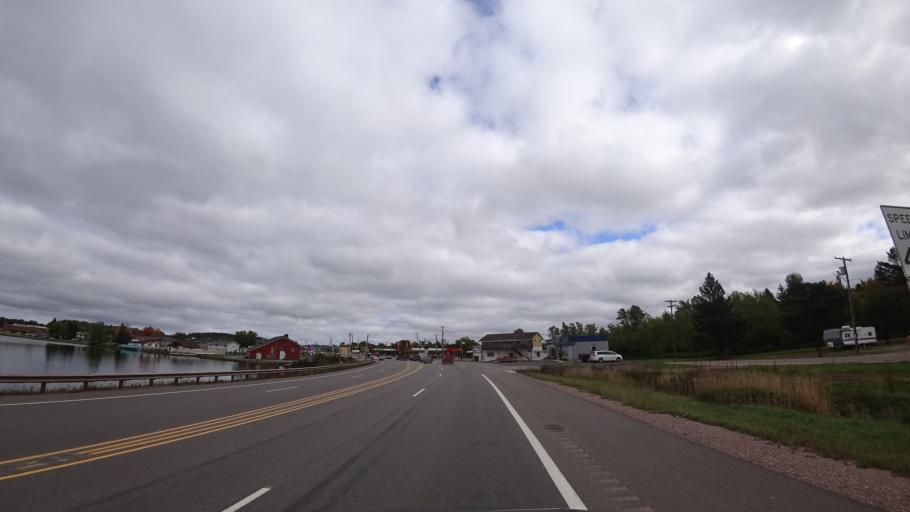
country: US
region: Michigan
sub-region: Marquette County
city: Negaunee
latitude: 46.5066
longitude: -87.6148
